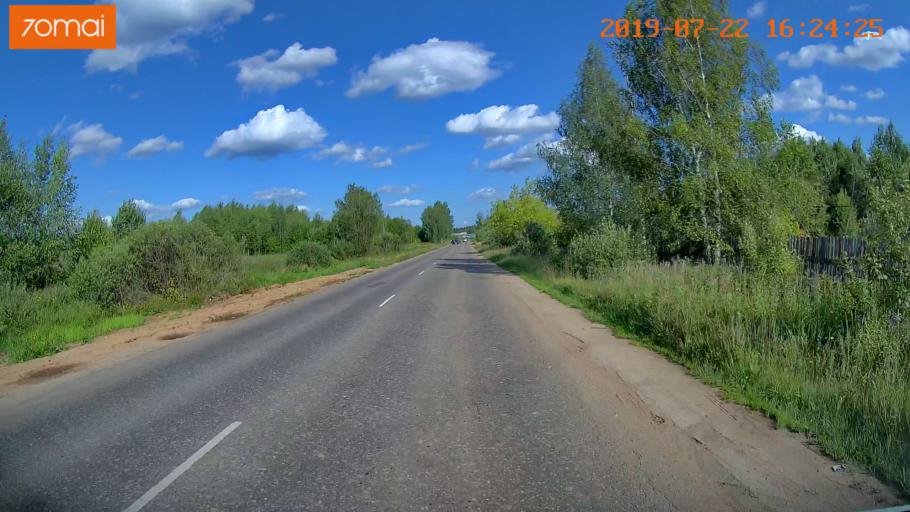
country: RU
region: Ivanovo
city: Novo-Talitsy
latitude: 57.0583
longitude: 40.9130
